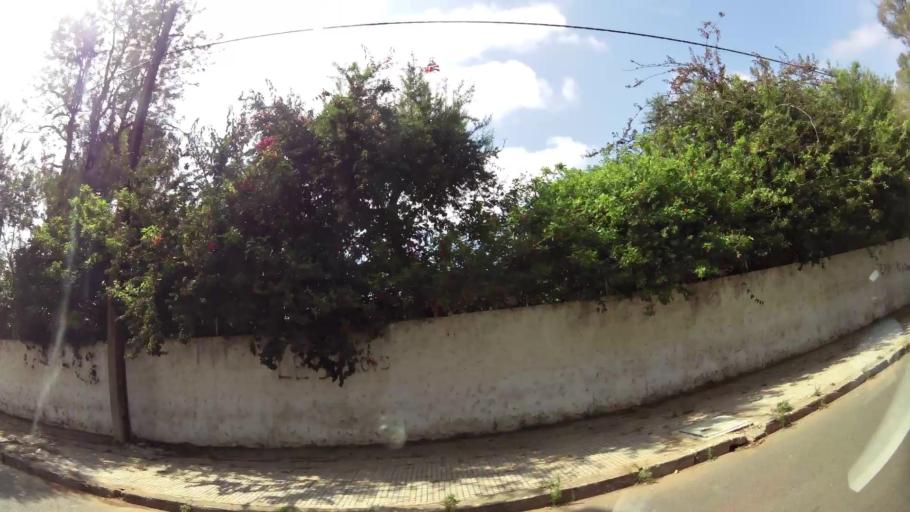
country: MA
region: Rabat-Sale-Zemmour-Zaer
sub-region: Rabat
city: Rabat
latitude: 33.9831
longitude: -6.8334
